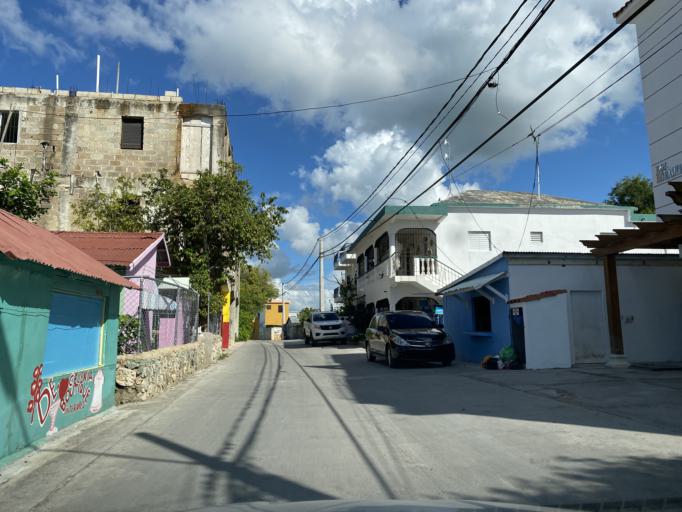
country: DO
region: La Romana
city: La Romana
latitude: 18.3691
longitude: -68.8379
